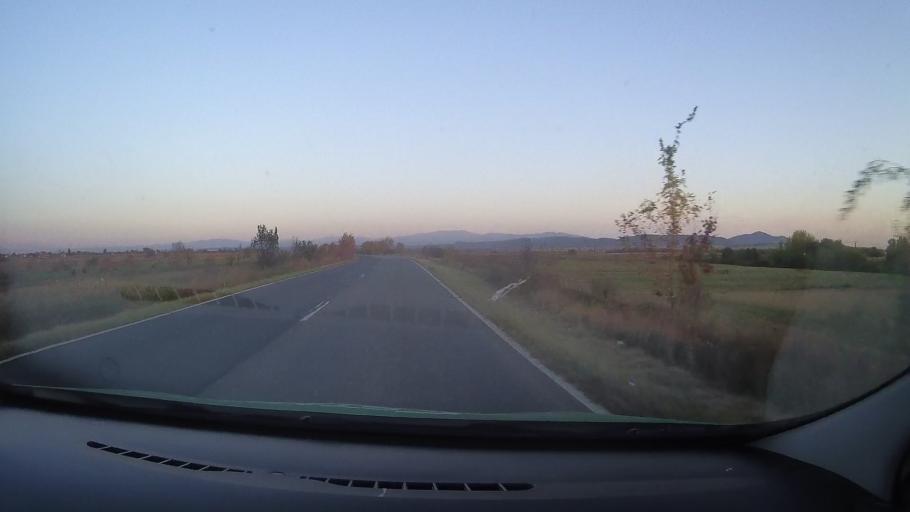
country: RO
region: Timis
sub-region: Comuna Dumbrava
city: Rachita
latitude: 45.8216
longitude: 22.0983
